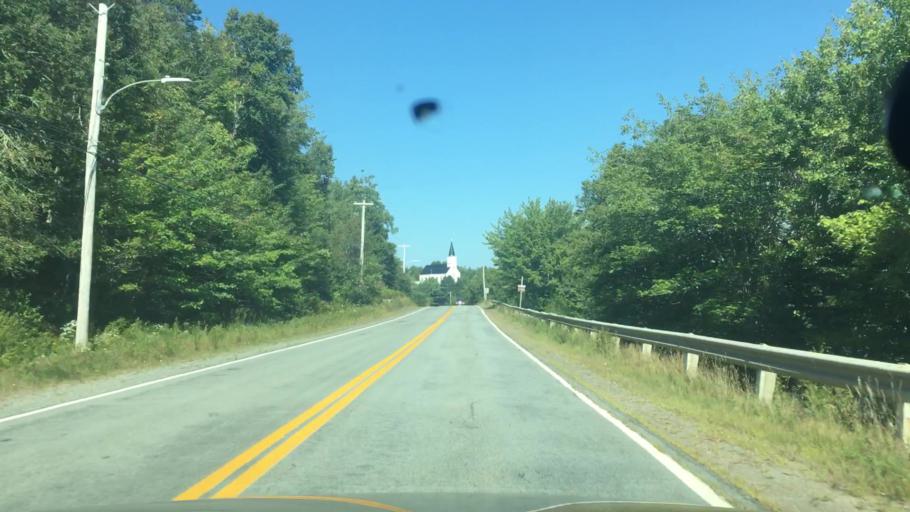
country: CA
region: Nova Scotia
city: New Glasgow
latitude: 44.9200
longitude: -62.5435
